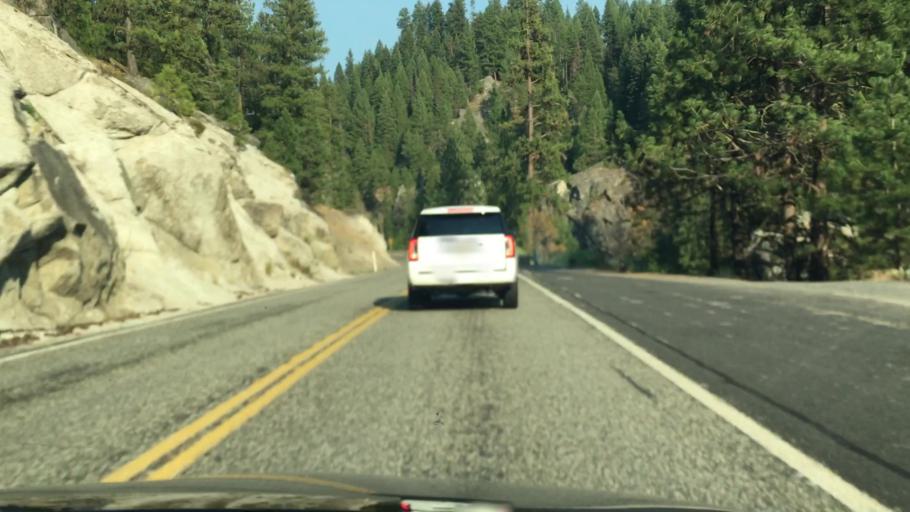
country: US
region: Idaho
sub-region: Valley County
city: Cascade
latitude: 44.3125
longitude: -116.0791
